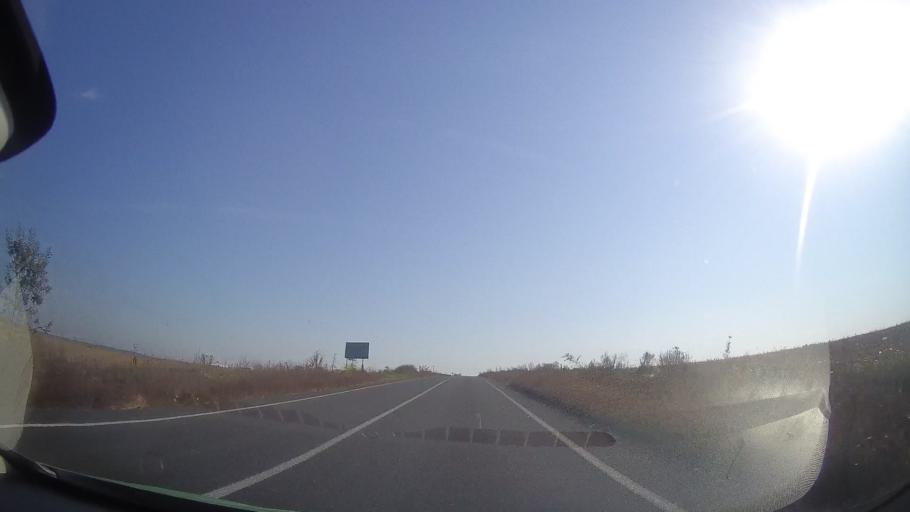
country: RO
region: Timis
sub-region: Comuna Topolovatu Mare
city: Topolovatu Mare
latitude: 45.7747
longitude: 21.6343
